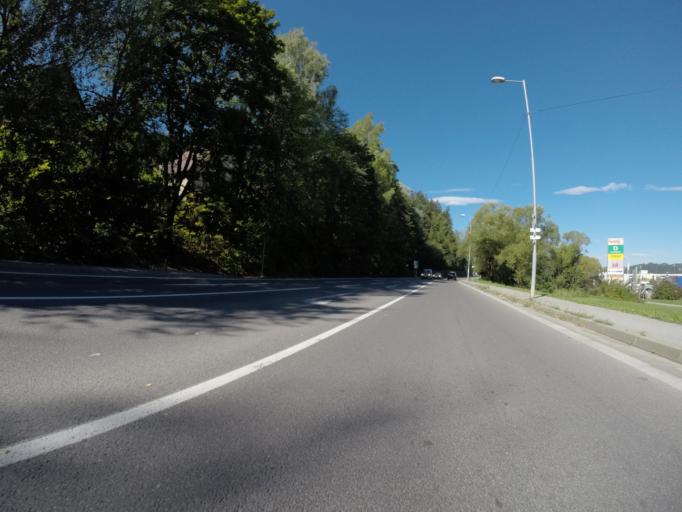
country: SK
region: Trenciansky
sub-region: Okres Povazska Bystrica
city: Povazska Bystrica
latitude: 49.1008
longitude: 18.4607
